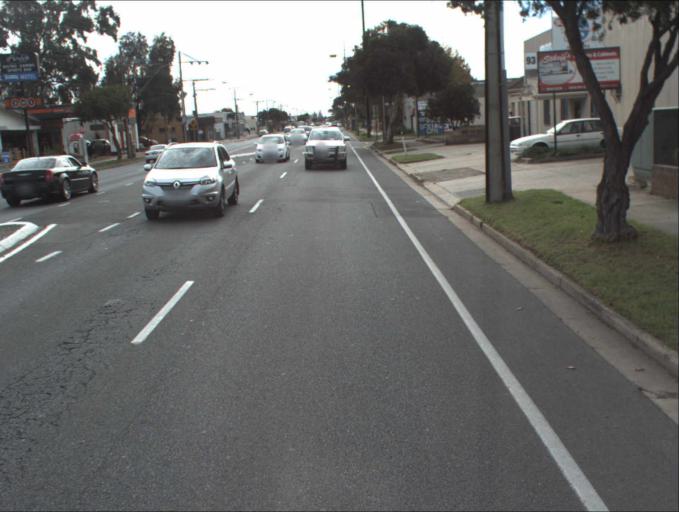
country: AU
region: South Australia
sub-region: Charles Sturt
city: Royal Park
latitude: -34.8749
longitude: 138.5125
